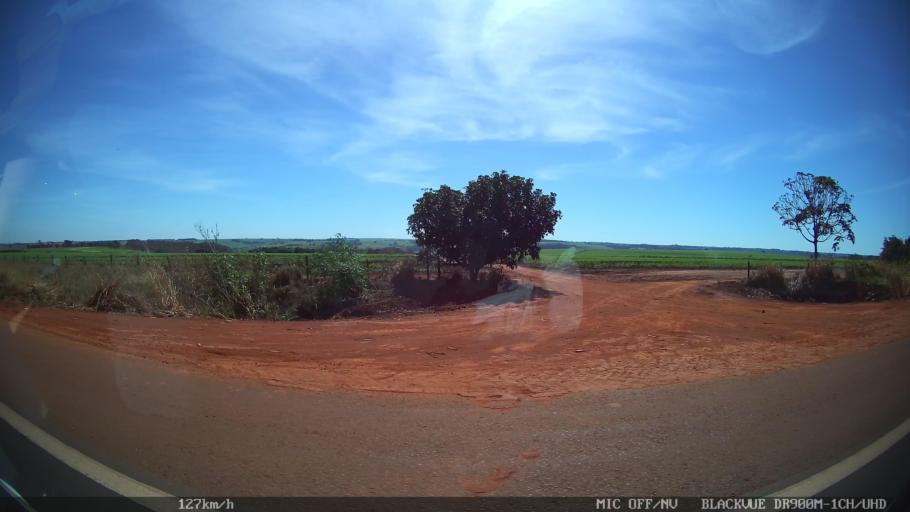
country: BR
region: Sao Paulo
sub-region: Franca
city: Franca
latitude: -20.5595
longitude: -47.6050
